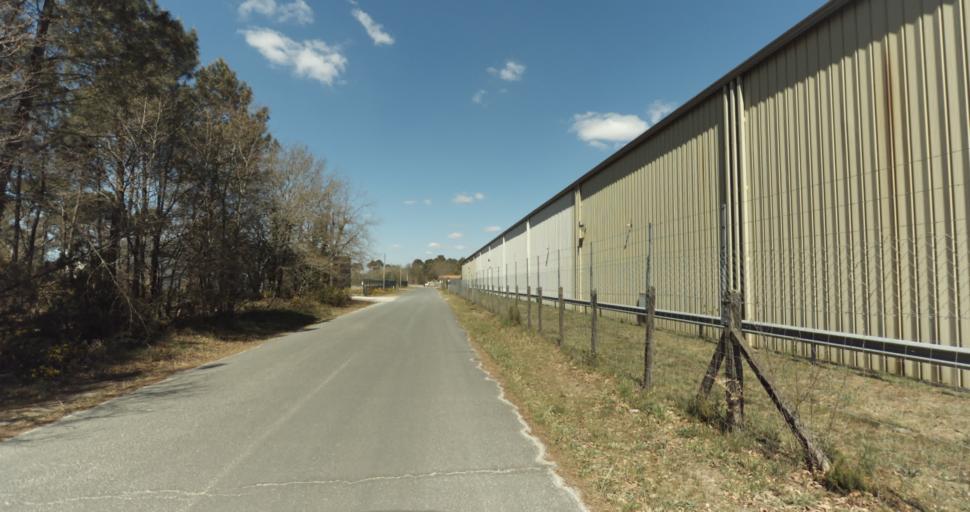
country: FR
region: Aquitaine
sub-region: Departement de la Gironde
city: Martignas-sur-Jalle
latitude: 44.8077
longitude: -0.7619
